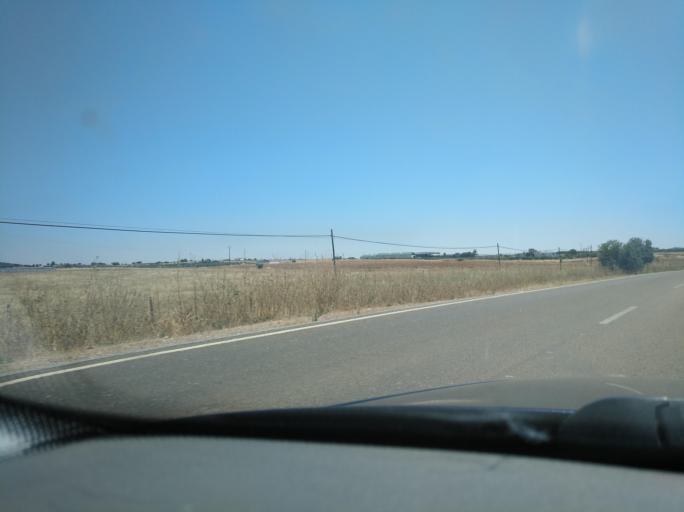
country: ES
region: Extremadura
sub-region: Provincia de Badajoz
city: Olivenza
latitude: 38.6949
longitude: -7.1276
